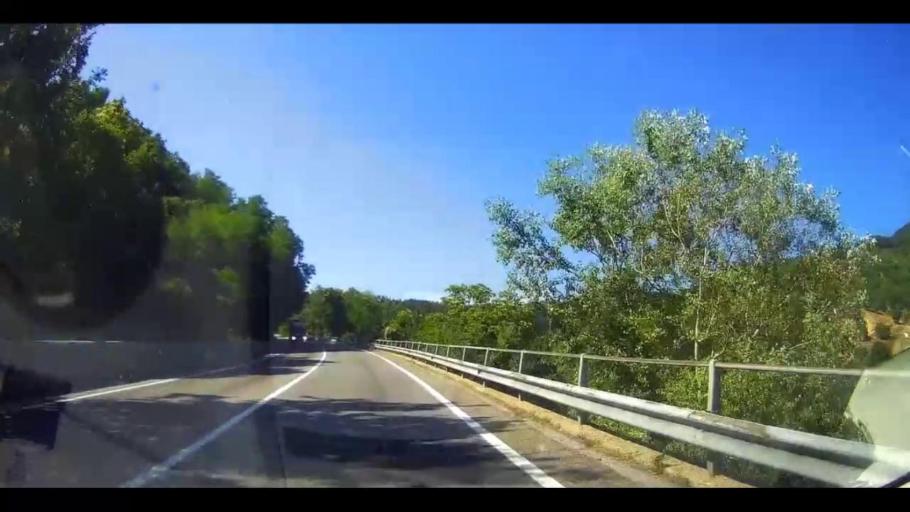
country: IT
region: Calabria
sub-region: Provincia di Cosenza
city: Spezzano Piccolo
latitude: 39.2968
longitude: 16.3549
